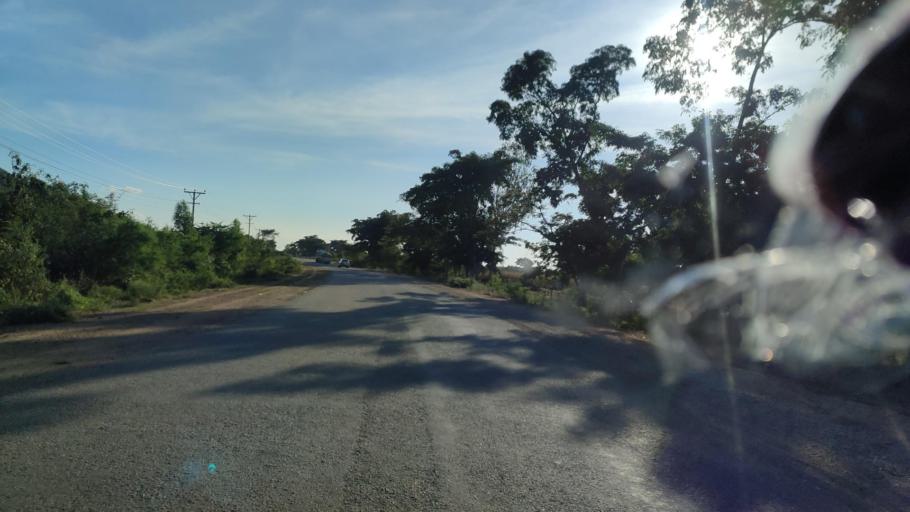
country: MM
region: Mandalay
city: Yamethin
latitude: 20.7353
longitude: 96.2062
